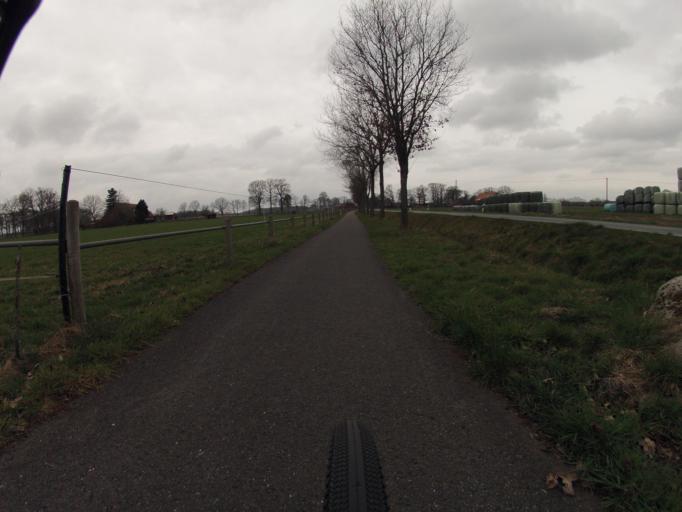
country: DE
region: North Rhine-Westphalia
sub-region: Regierungsbezirk Munster
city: Mettingen
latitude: 52.3469
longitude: 7.8032
